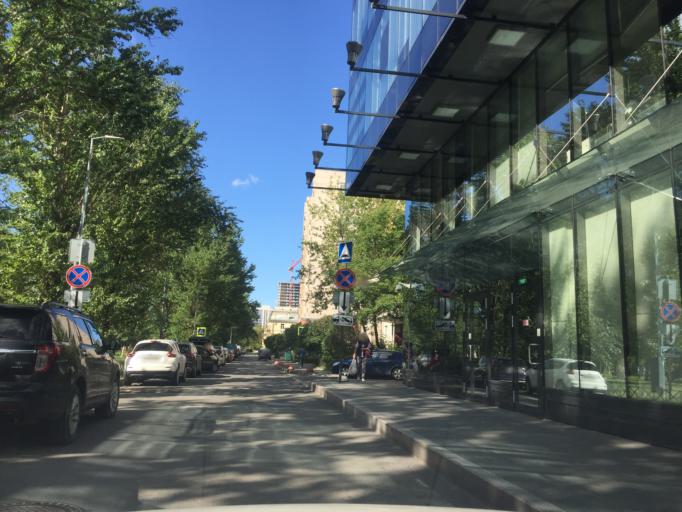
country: RU
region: St.-Petersburg
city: Kupchino
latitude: 59.8257
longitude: 30.3258
